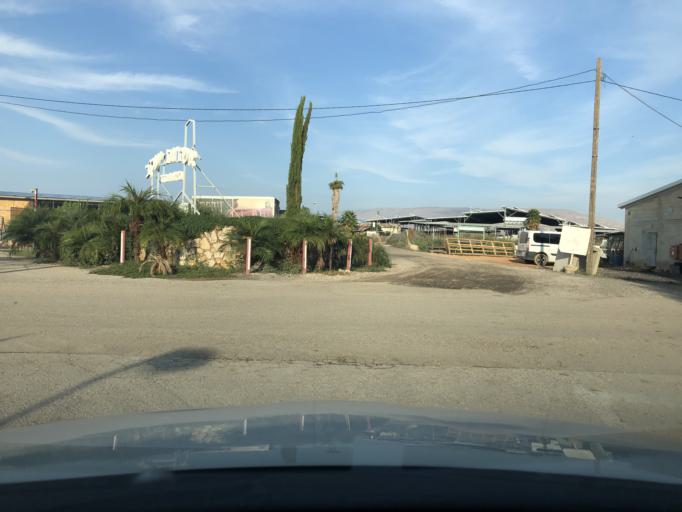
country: IL
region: Northern District
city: Yavne'el
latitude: 32.6643
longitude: 35.5813
